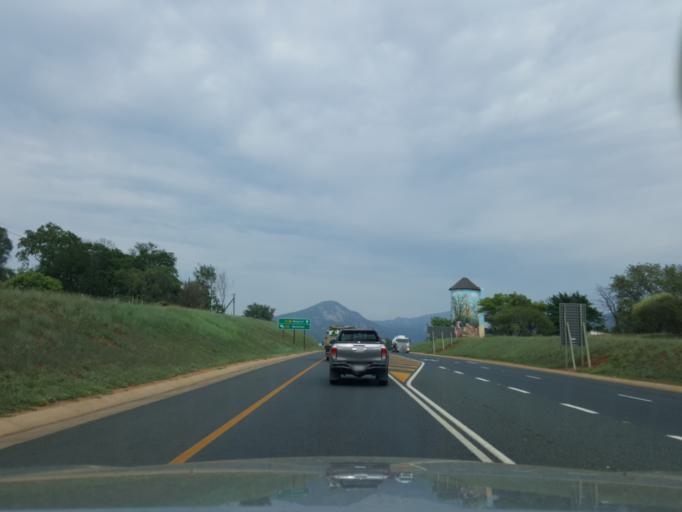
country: SZ
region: Hhohho
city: Ntfonjeni
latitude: -25.5368
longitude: 31.3326
